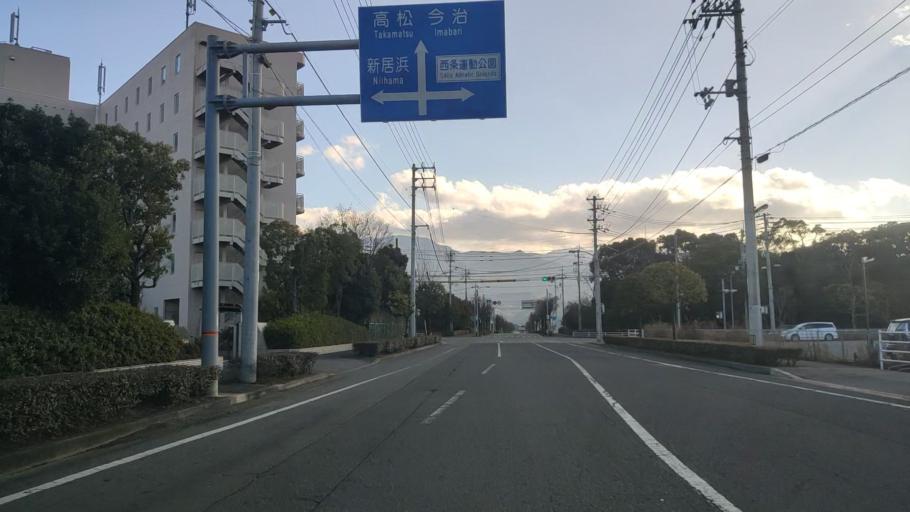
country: JP
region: Ehime
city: Saijo
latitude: 33.9360
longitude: 133.1923
